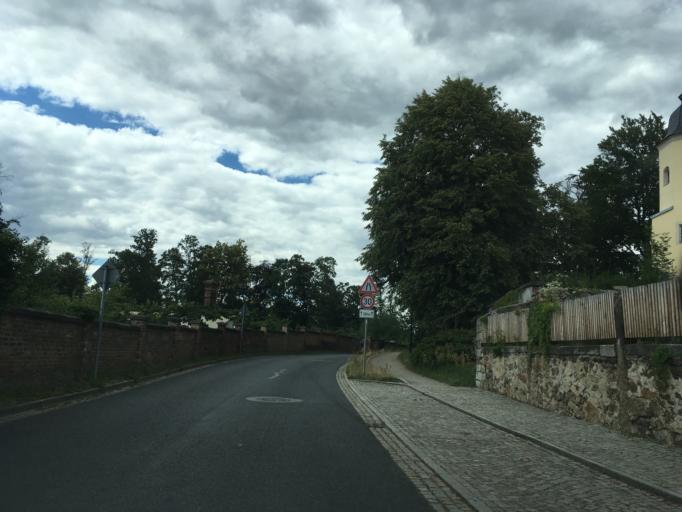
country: DE
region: Saxony
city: Wachau
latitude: 51.1573
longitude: 13.9044
